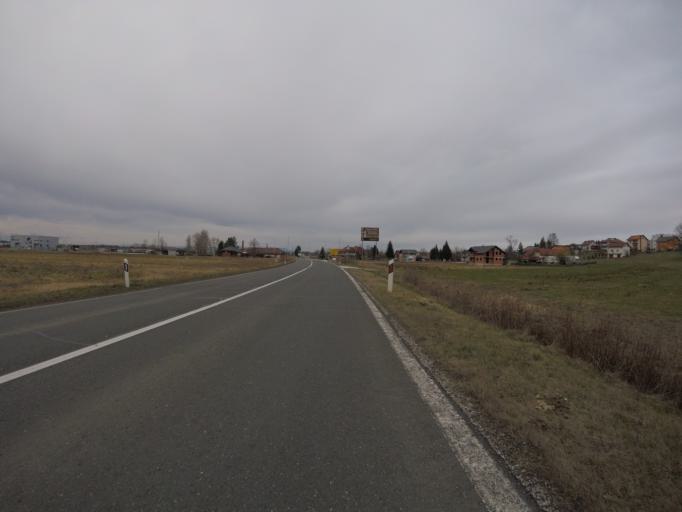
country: HR
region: Grad Zagreb
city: Horvati
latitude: 45.5829
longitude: 15.8580
